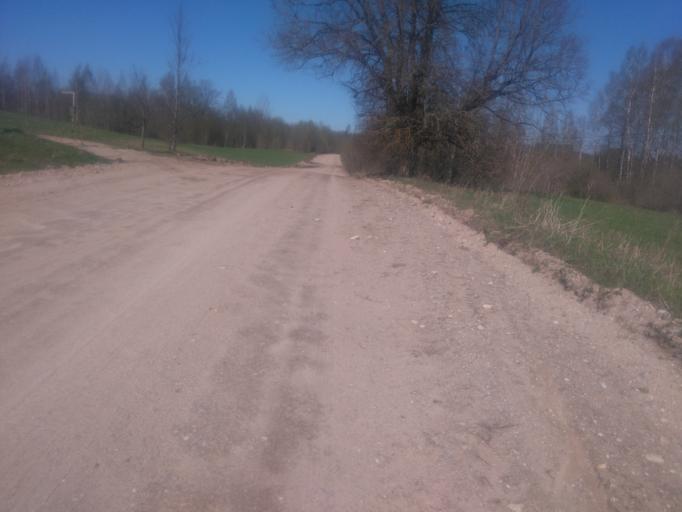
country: LV
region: Vecpiebalga
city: Vecpiebalga
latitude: 57.0259
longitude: 25.8402
